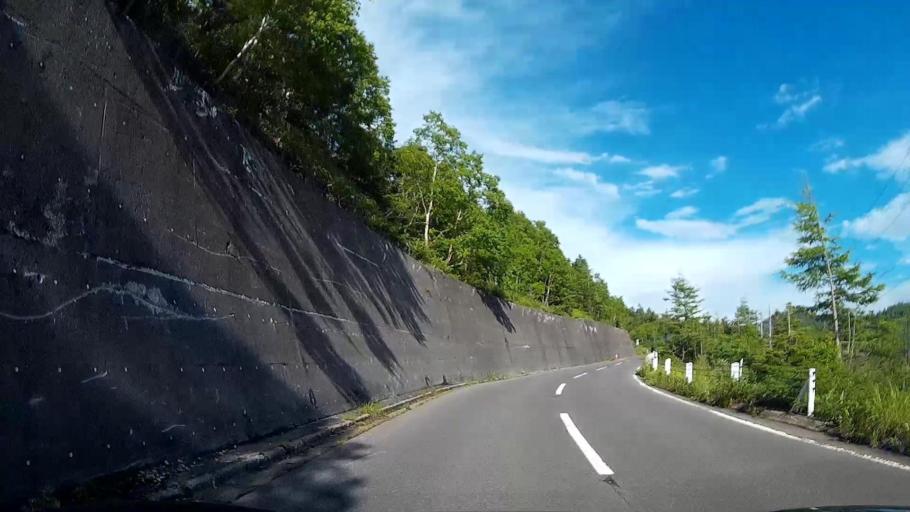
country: JP
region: Nagano
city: Nakano
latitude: 36.6396
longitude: 138.5266
